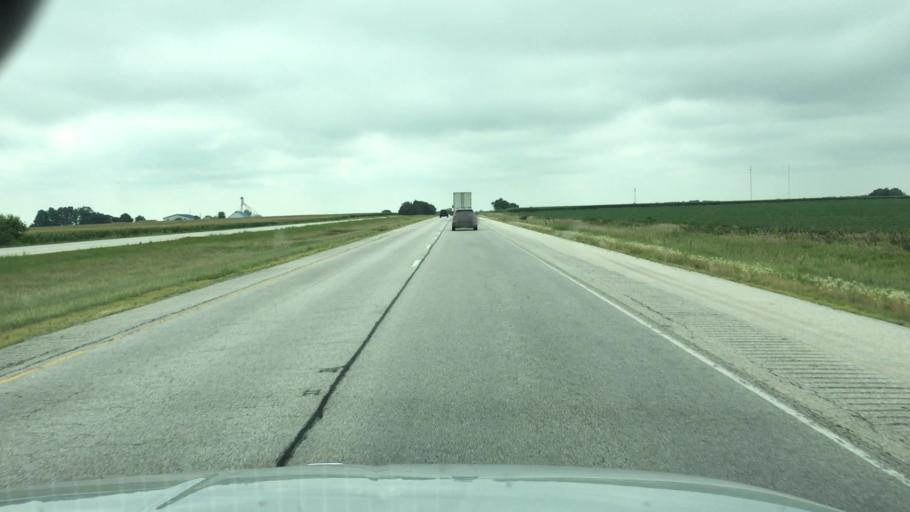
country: US
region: Illinois
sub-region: Knox County
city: Galesburg
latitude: 41.1004
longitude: -90.3330
